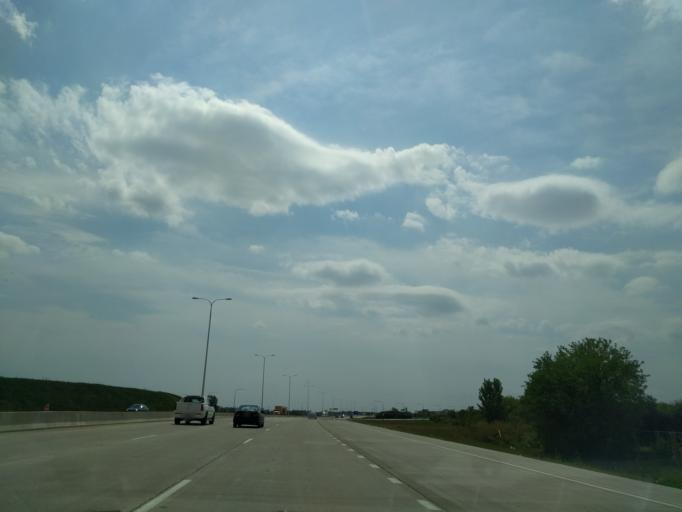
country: US
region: Illinois
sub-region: Cook County
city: Rosemont
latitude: 41.9878
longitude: -87.8789
